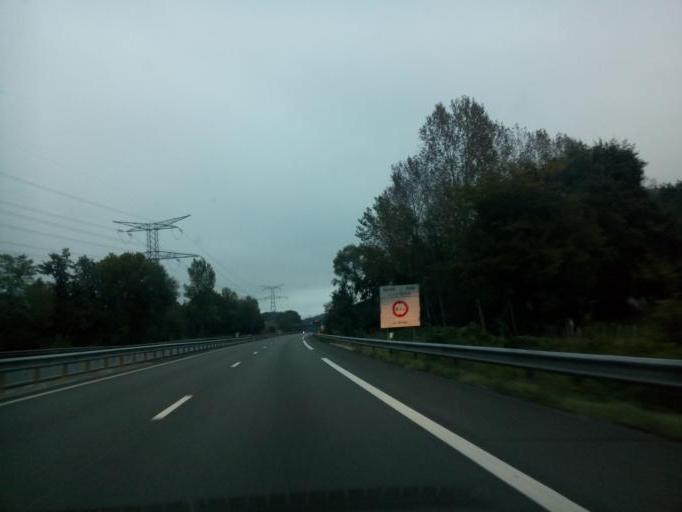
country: FR
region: Rhone-Alpes
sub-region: Departement de l'Isere
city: Fitilieu
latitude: 45.5706
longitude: 5.5626
